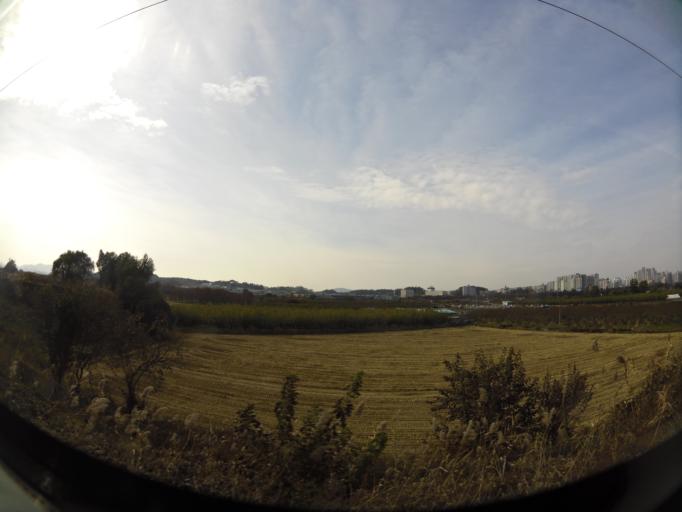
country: KR
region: Daejeon
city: Songgang-dong
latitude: 36.5871
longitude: 127.3064
